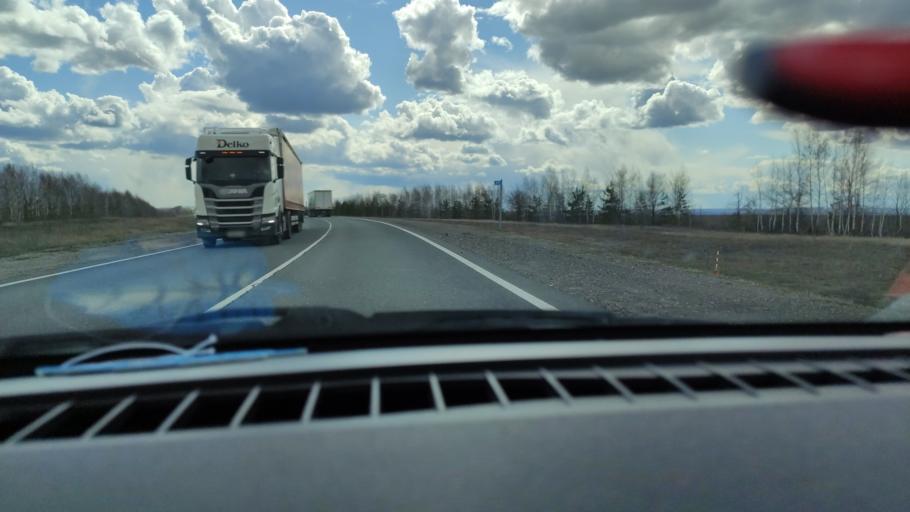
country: RU
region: Saratov
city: Dukhovnitskoye
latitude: 52.8314
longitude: 48.2394
